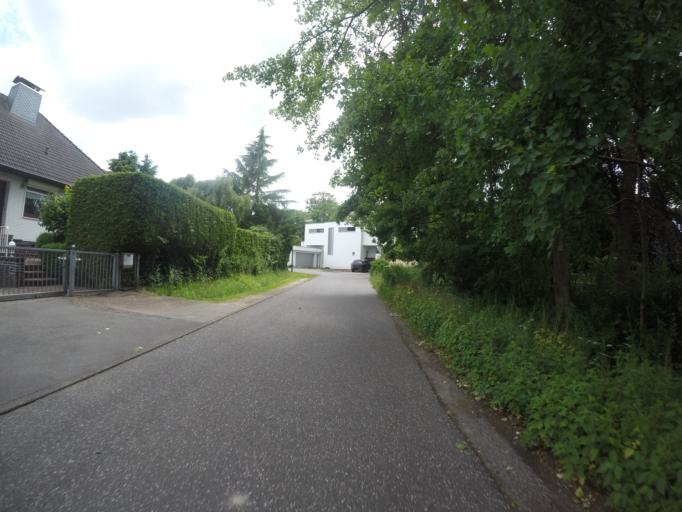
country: DE
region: Hamburg
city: Langenhorn
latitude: 53.6443
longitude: 9.9719
